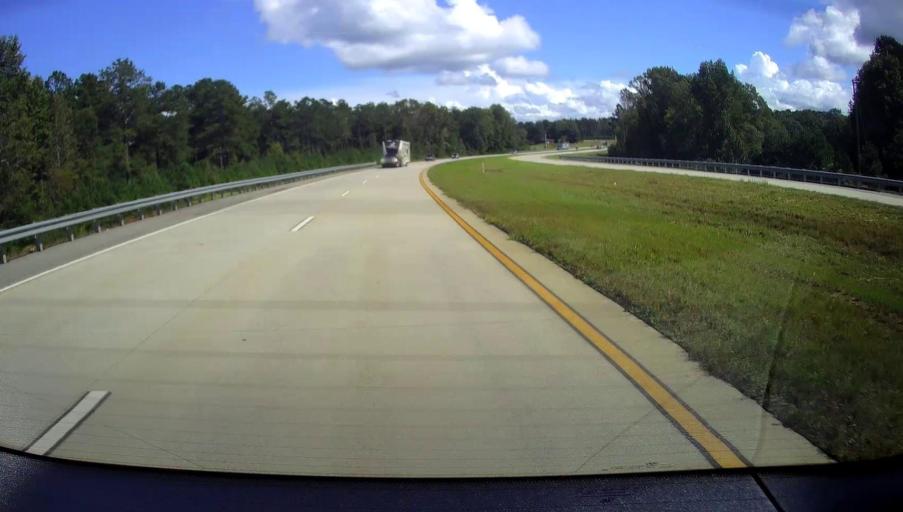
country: US
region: Georgia
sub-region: Jones County
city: Gray
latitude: 33.0296
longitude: -83.5266
